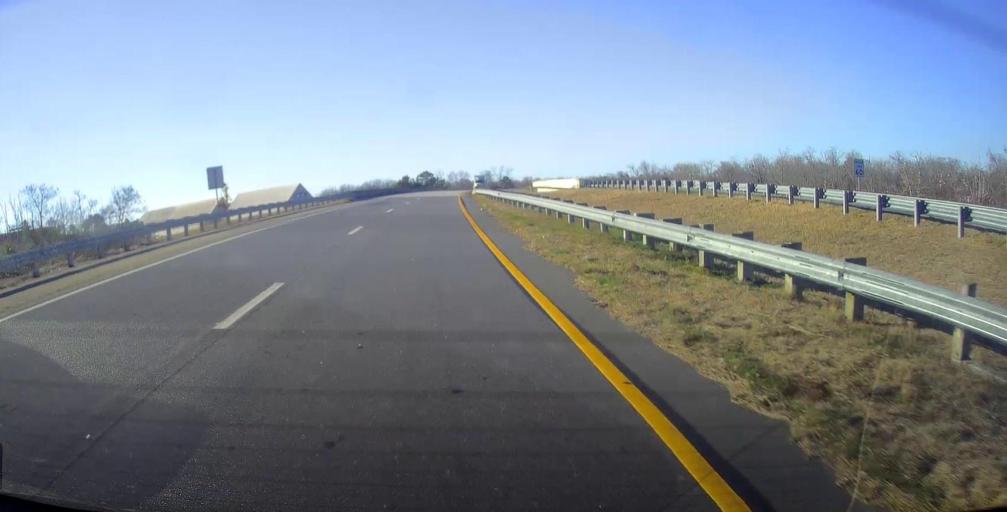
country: US
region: Georgia
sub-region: Sumter County
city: Americus
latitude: 31.8951
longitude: -84.2607
